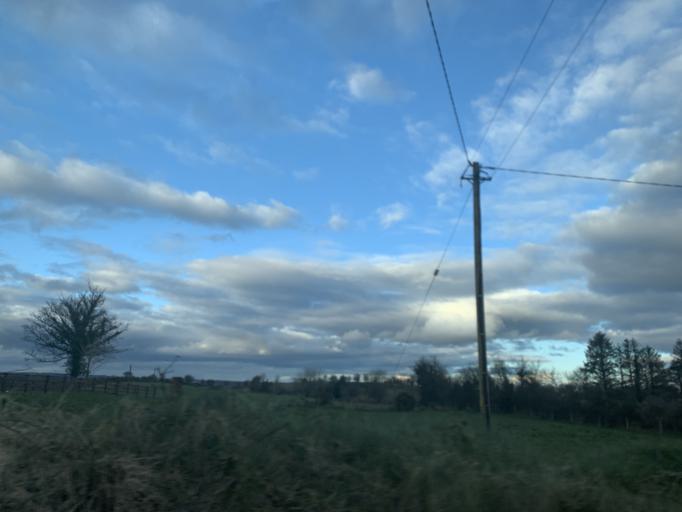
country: IE
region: Connaught
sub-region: Maigh Eo
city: Ballyhaunis
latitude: 53.8572
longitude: -8.7372
